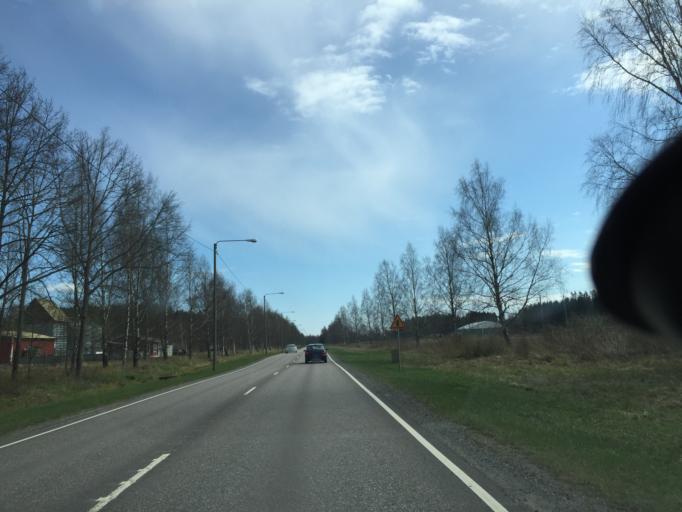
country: FI
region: Uusimaa
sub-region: Raaseporin
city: Ekenaes
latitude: 59.9983
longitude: 23.4052
